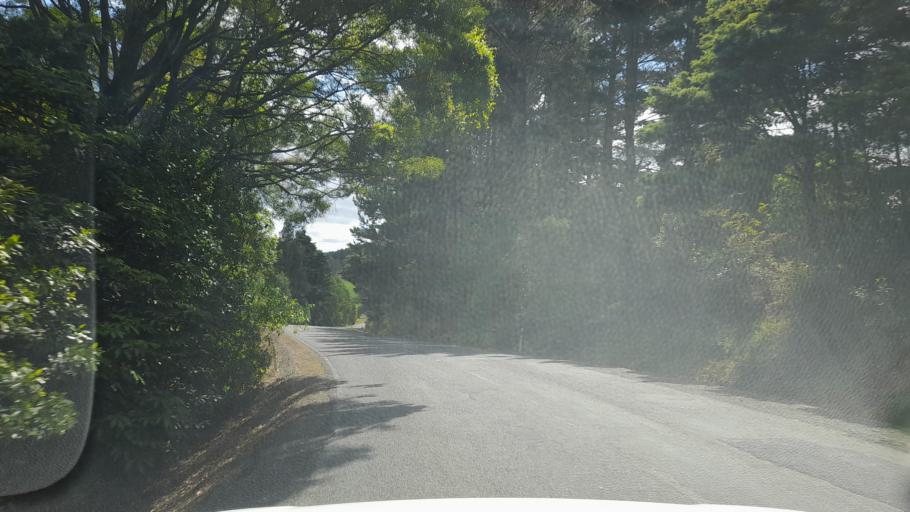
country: NZ
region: Northland
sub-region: Whangarei
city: Maungatapere
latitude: -35.7130
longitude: 174.0625
